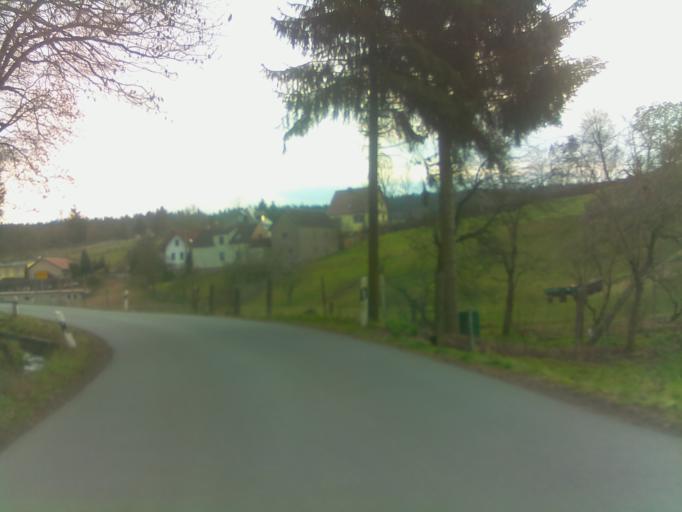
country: DE
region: Thuringia
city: Unterbodnitz
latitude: 50.8137
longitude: 11.6552
